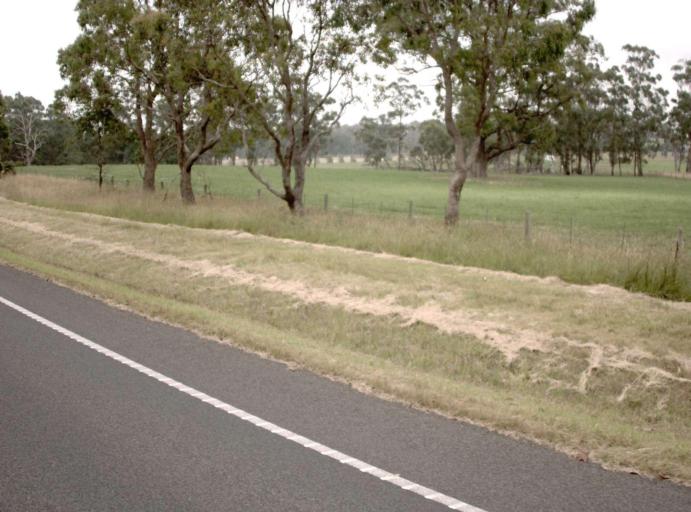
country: AU
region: Victoria
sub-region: Latrobe
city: Morwell
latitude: -38.2852
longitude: 146.3188
